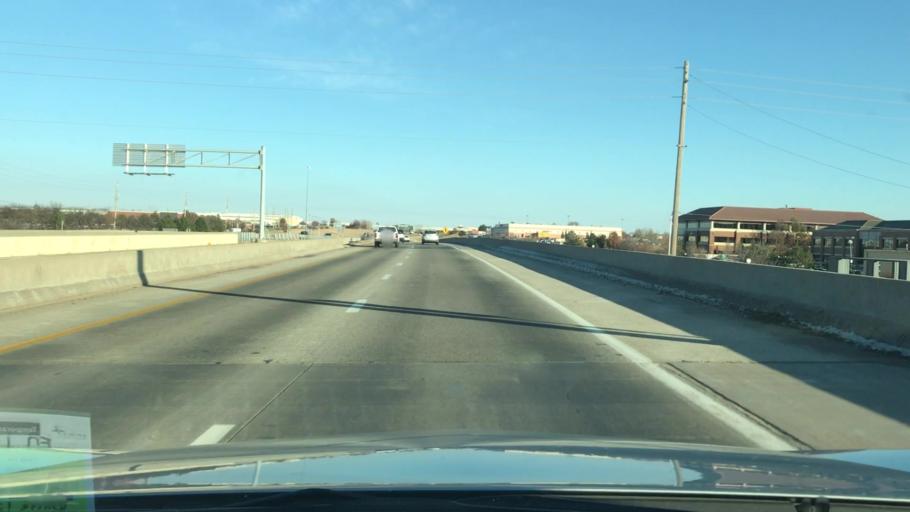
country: US
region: Kansas
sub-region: Sedgwick County
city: Bellaire
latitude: 37.7443
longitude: -97.2444
